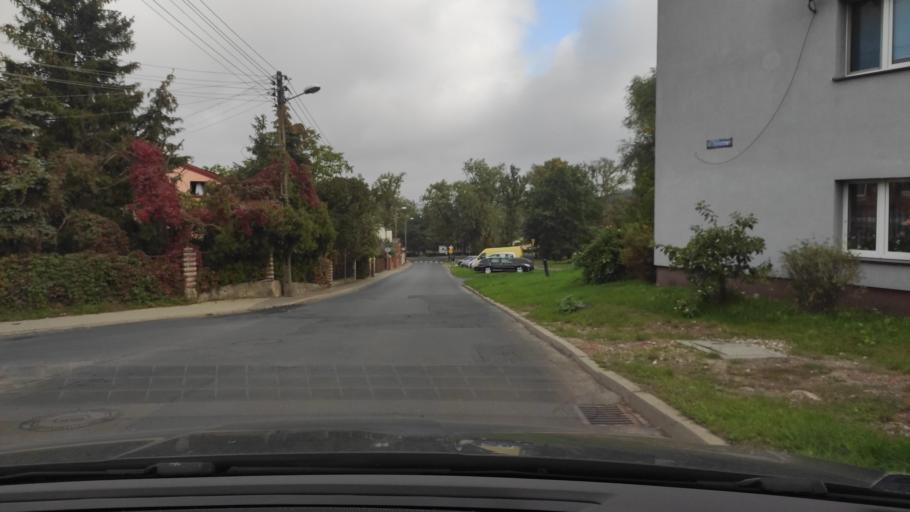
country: PL
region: Greater Poland Voivodeship
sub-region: Powiat poznanski
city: Swarzedz
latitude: 52.4082
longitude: 17.0701
